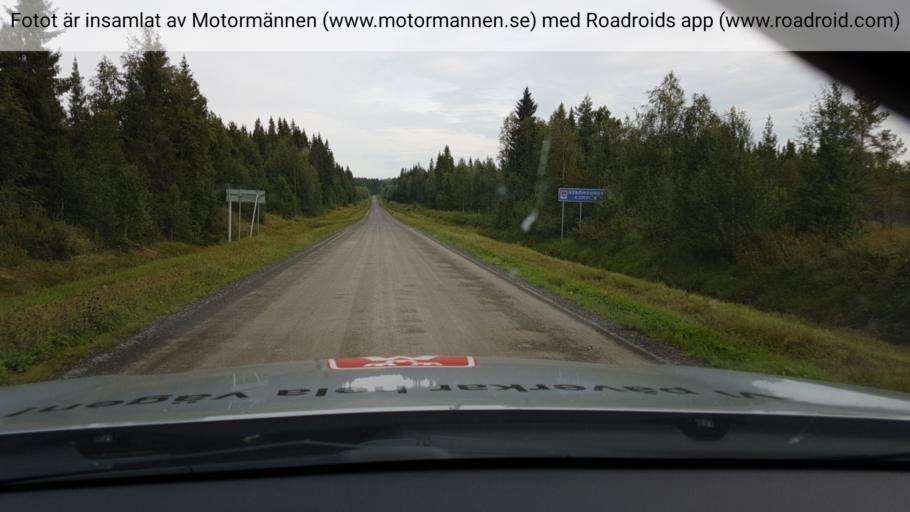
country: SE
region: Jaemtland
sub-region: OEstersunds Kommun
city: Lit
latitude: 63.6520
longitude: 14.9364
